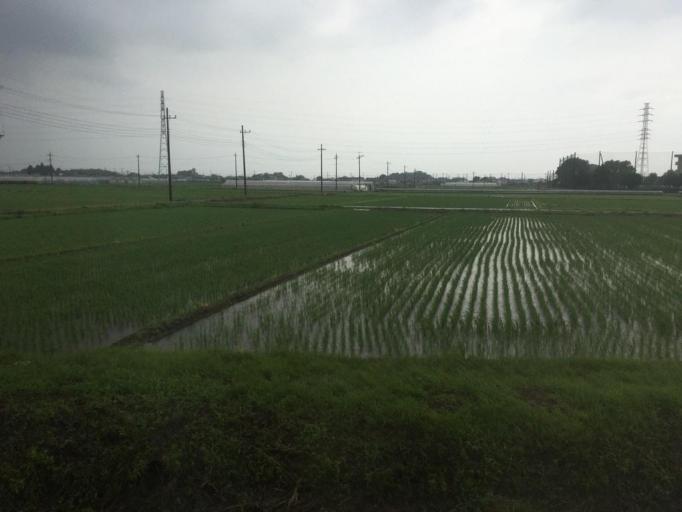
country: JP
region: Tochigi
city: Ashikaga
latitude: 36.2946
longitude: 139.4659
